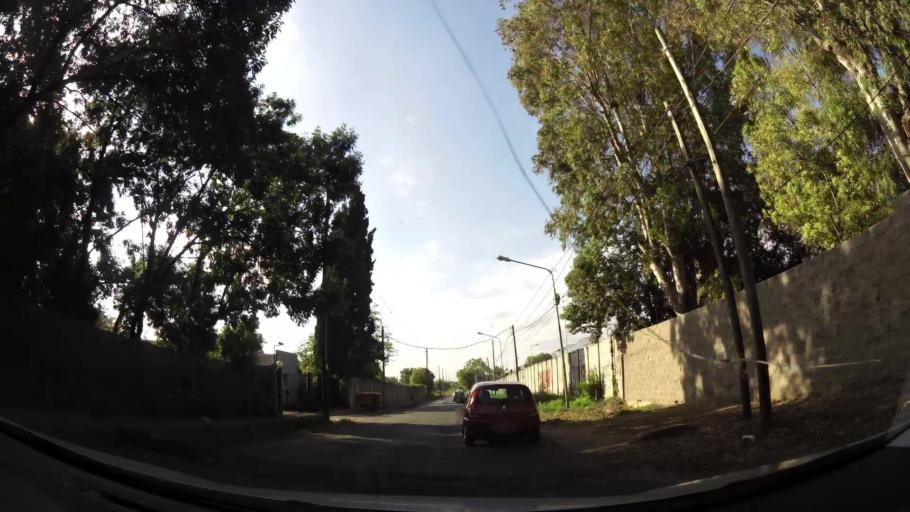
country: AR
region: Buenos Aires
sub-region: Partido de Tigre
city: Tigre
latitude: -34.4717
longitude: -58.6636
